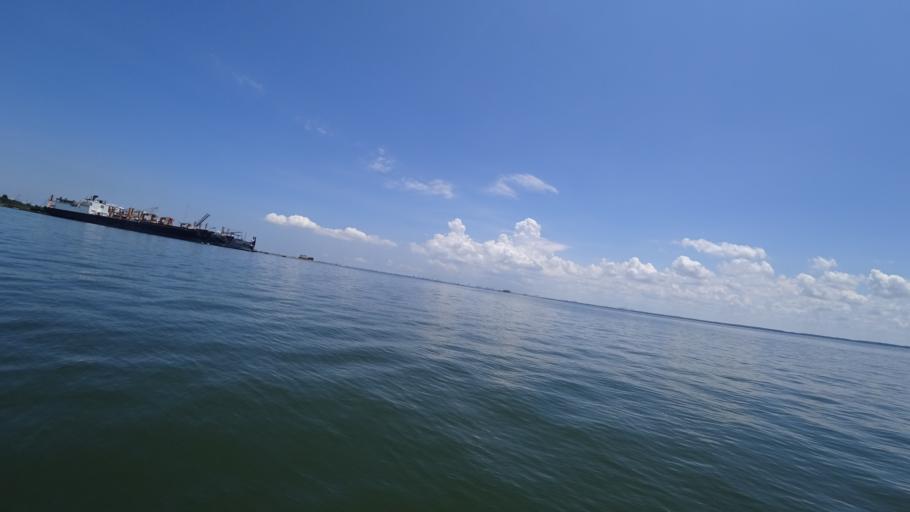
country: US
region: Virginia
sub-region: City of Newport News
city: Newport News
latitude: 36.9605
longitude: -76.4274
